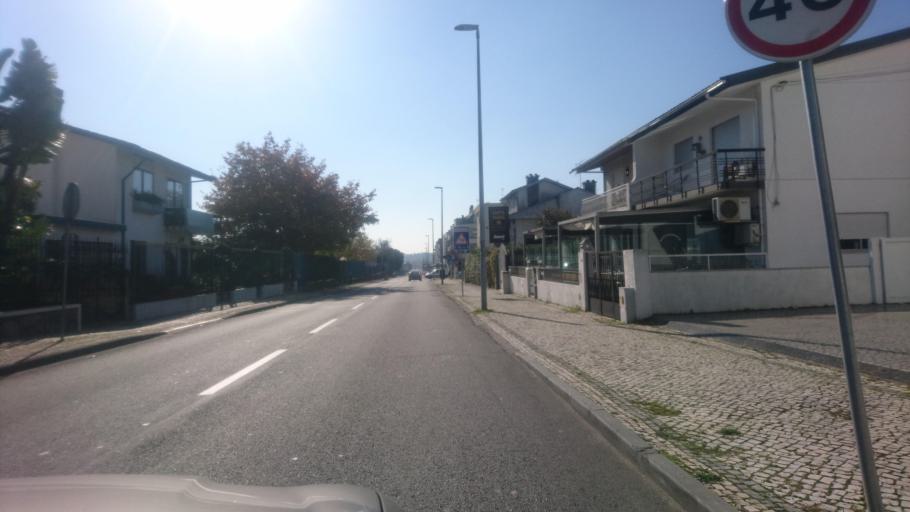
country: PT
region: Aveiro
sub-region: Santa Maria da Feira
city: Feira
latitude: 40.9253
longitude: -8.5582
